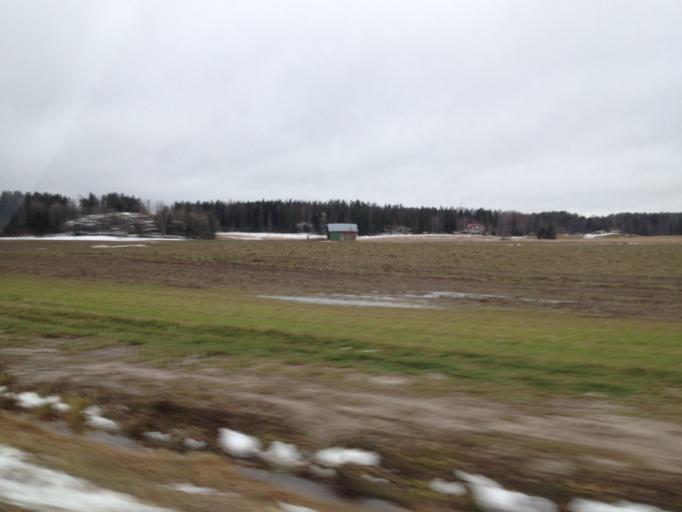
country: FI
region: Uusimaa
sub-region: Raaseporin
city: Karis
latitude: 60.0914
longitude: 23.7800
